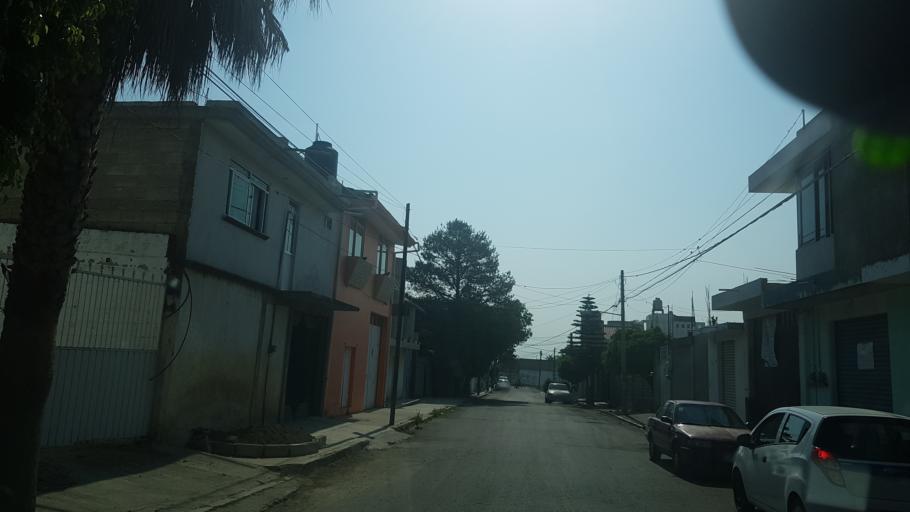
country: MX
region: Puebla
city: Nealtican
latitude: 19.0511
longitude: -98.4229
